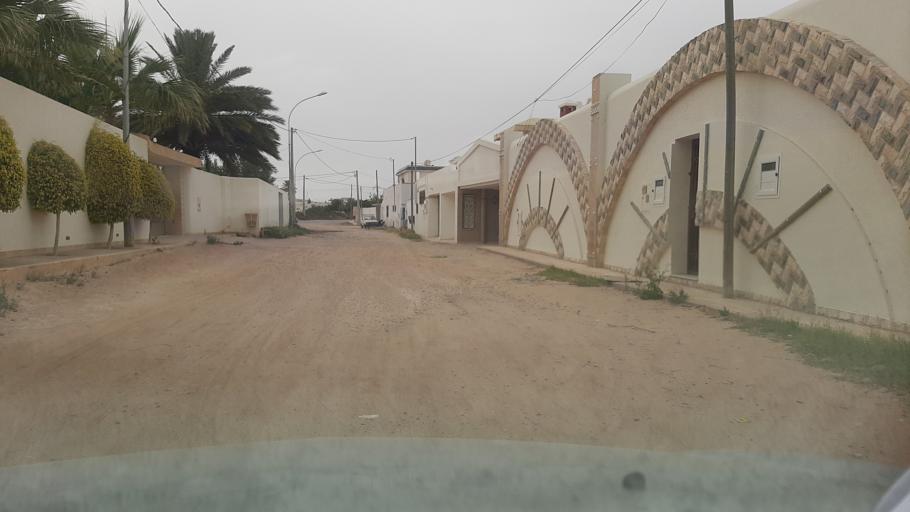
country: TN
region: Safaqis
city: Al Qarmadah
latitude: 34.7916
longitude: 10.7644
